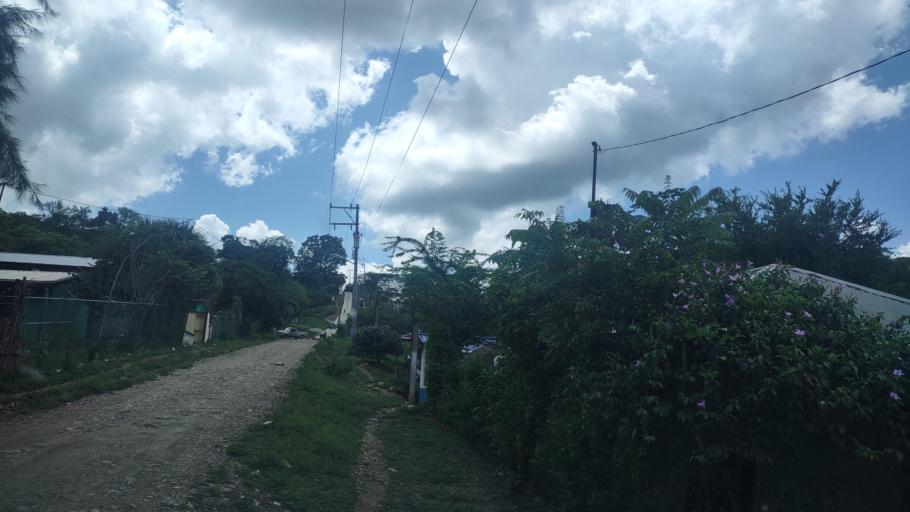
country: MX
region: Veracruz
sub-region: Tantoyuca
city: El Lindero
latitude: 21.3019
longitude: -98.1322
